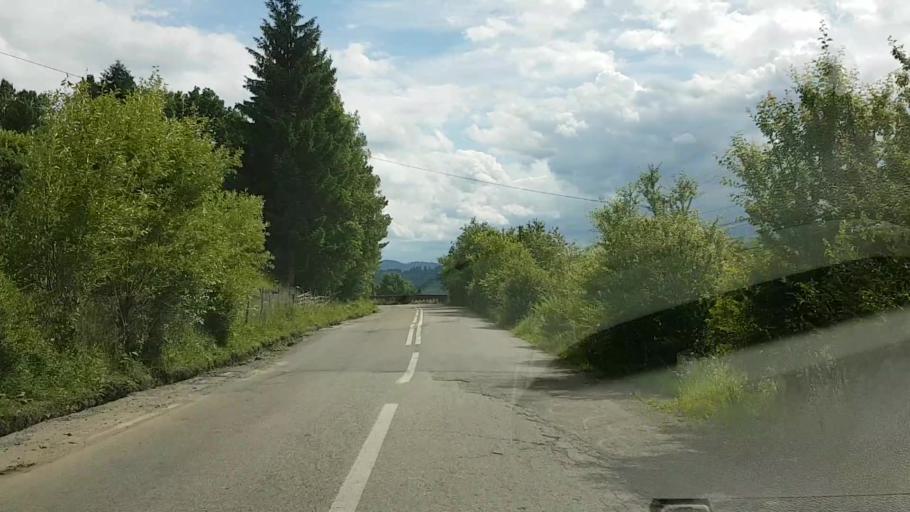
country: RO
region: Neamt
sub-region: Comuna Hangu
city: Hangu
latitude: 47.0312
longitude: 26.0662
